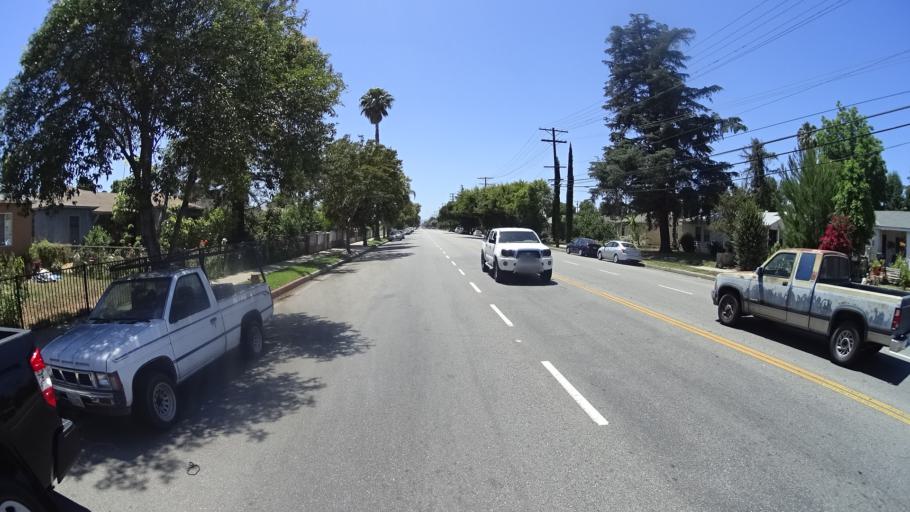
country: US
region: California
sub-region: Los Angeles County
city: Northridge
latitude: 34.1940
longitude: -118.5203
